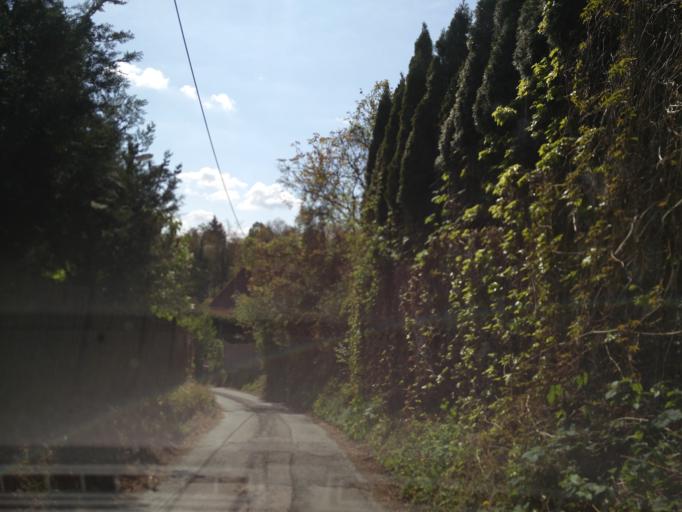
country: HU
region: Zala
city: Zalaegerszeg
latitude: 46.8252
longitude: 16.8386
